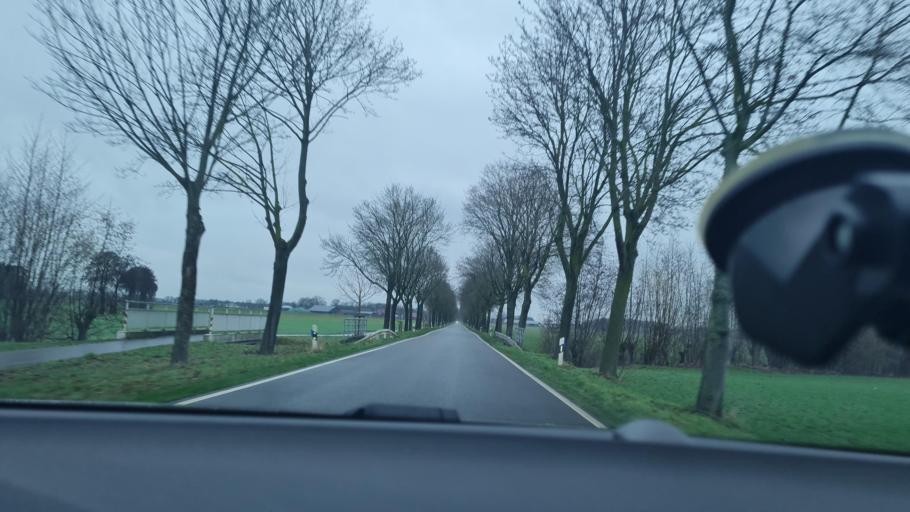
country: DE
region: North Rhine-Westphalia
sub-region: Regierungsbezirk Munster
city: Heiden
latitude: 51.7698
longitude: 6.9259
